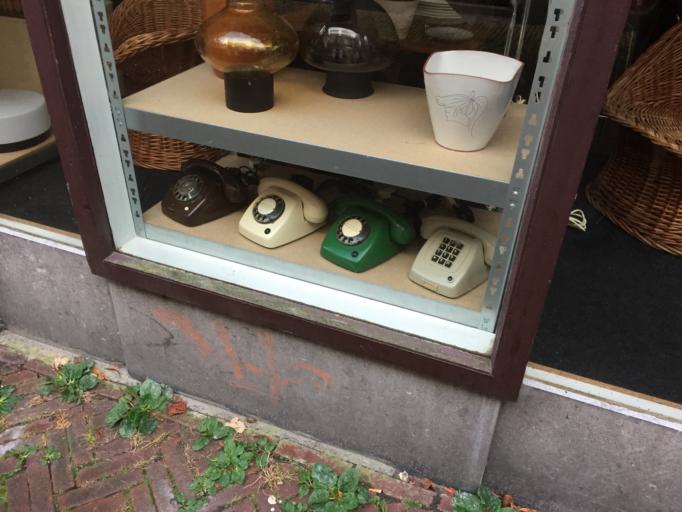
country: NL
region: Friesland
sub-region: Gemeente Leeuwarden
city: Leeuwarden
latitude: 53.2036
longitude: 5.7987
